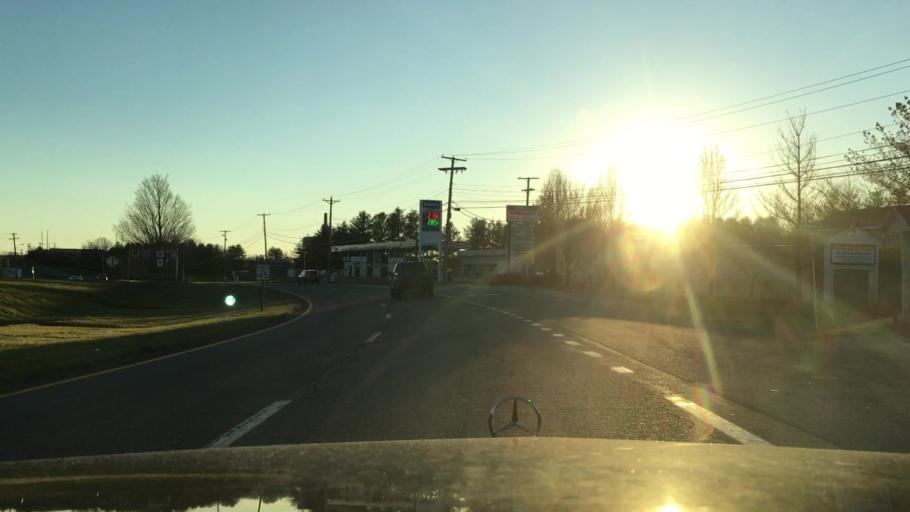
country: US
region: Virginia
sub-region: Montgomery County
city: Merrimac
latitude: 37.1755
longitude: -80.4191
